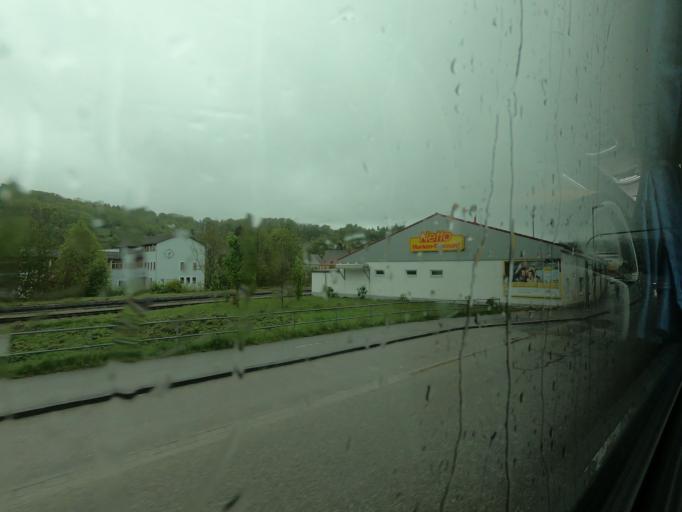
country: DE
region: Baden-Wuerttemberg
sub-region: Regierungsbezirk Stuttgart
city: Konigsbronn
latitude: 48.7385
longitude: 10.1187
